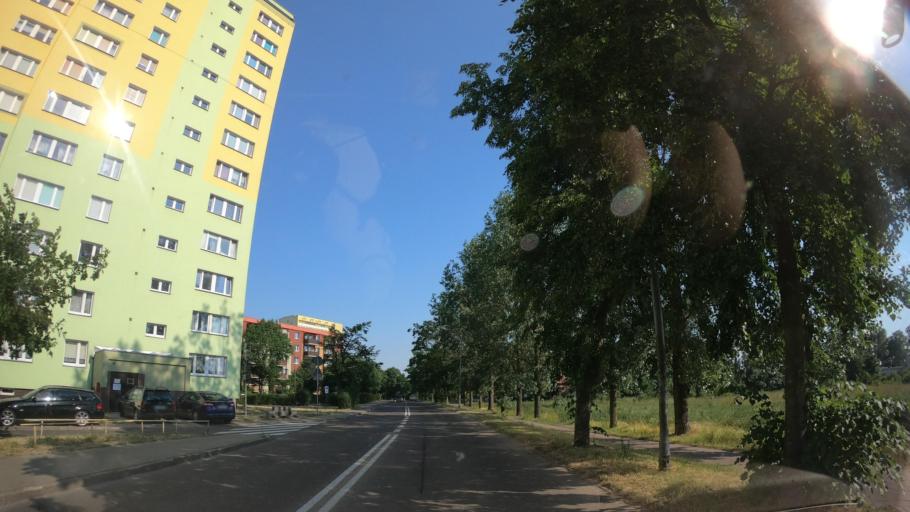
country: PL
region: West Pomeranian Voivodeship
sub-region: Powiat stargardzki
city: Stargard Szczecinski
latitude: 53.3399
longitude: 15.0032
